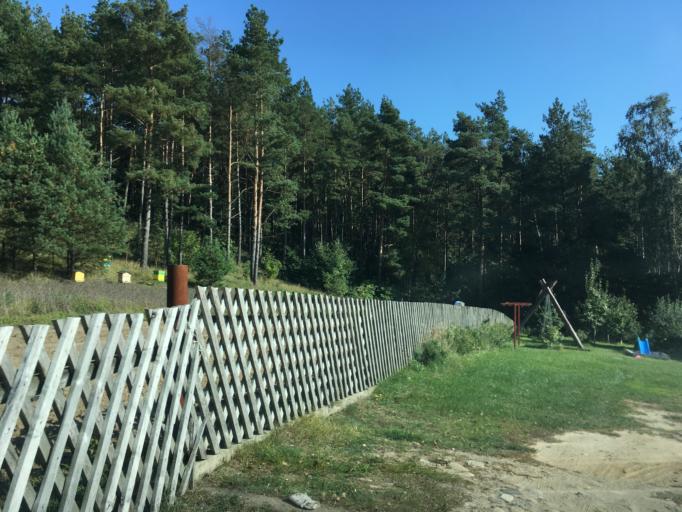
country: PL
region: Kujawsko-Pomorskie
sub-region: Powiat brodnicki
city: Bartniczka
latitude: 53.2647
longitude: 19.6770
